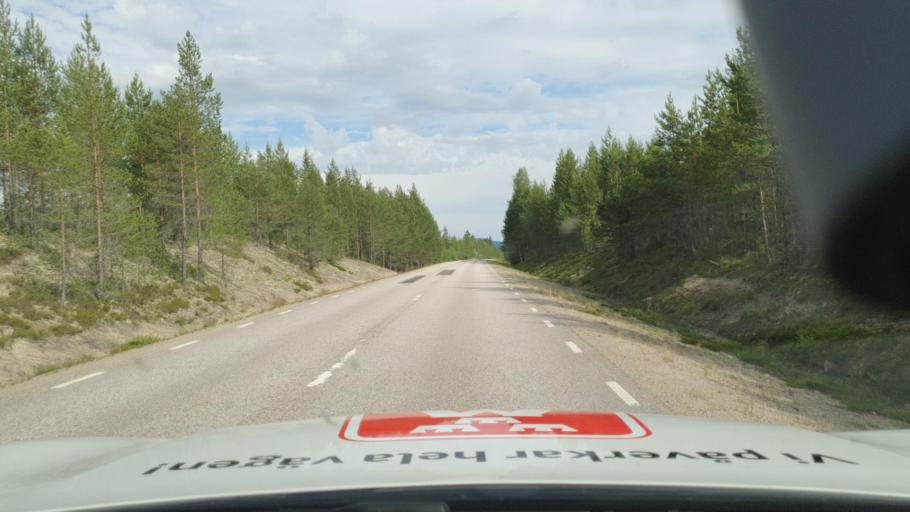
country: NO
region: Hedmark
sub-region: Trysil
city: Innbygda
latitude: 60.9247
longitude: 12.5223
